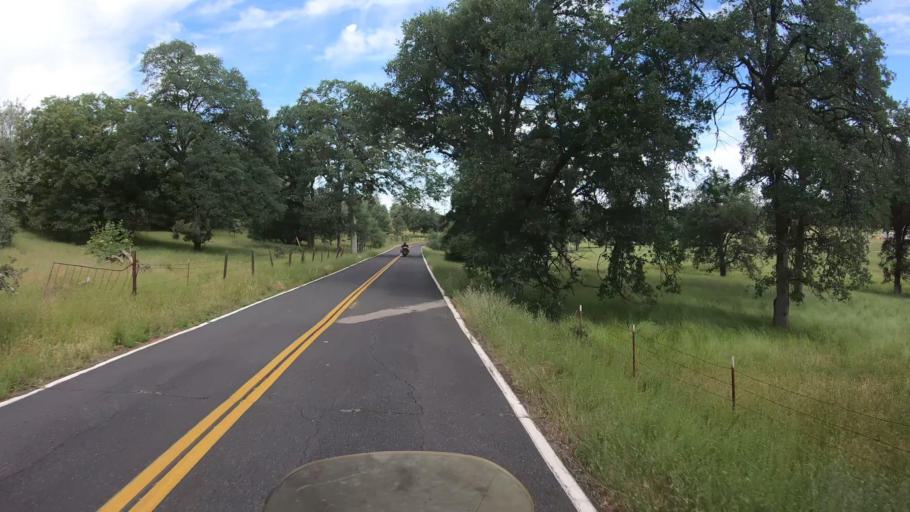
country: US
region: California
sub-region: Tuolumne County
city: Tuolumne City
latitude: 37.8481
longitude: -120.1433
